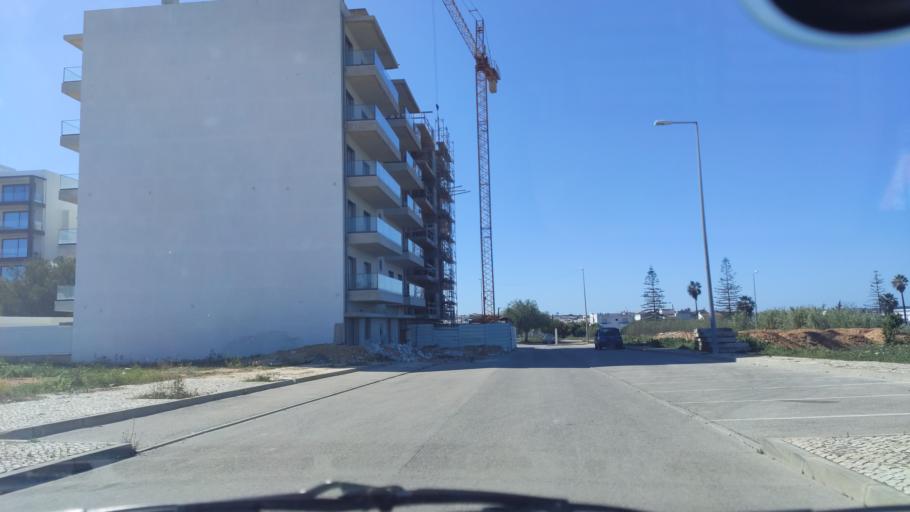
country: PT
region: Faro
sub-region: Faro
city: Faro
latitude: 37.0336
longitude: -7.9377
